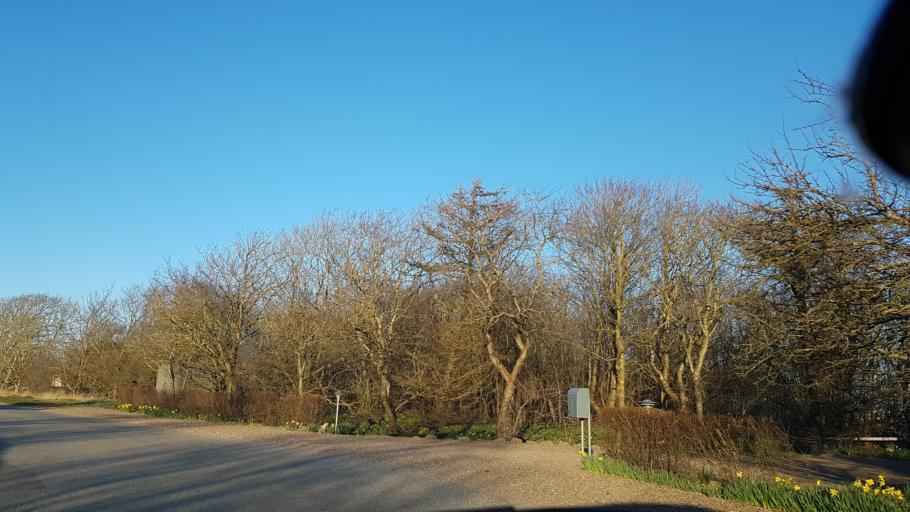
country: DK
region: South Denmark
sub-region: Esbjerg Kommune
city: Ribe
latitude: 55.3882
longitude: 8.7132
